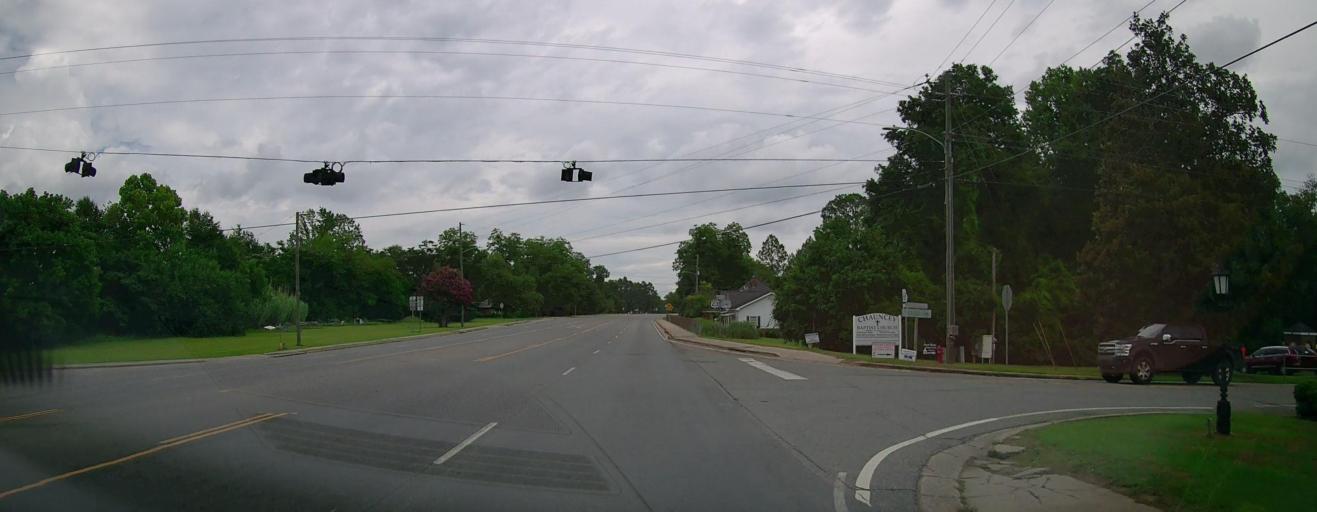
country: US
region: Georgia
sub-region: Dodge County
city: Eastman
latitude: 32.1047
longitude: -83.0657
